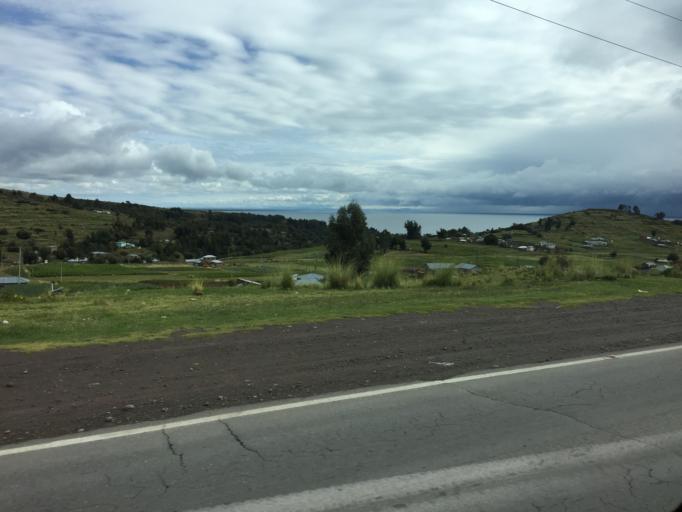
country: PE
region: Puno
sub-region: Provincia de Chucuito
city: Juli
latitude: -16.2017
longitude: -69.4196
